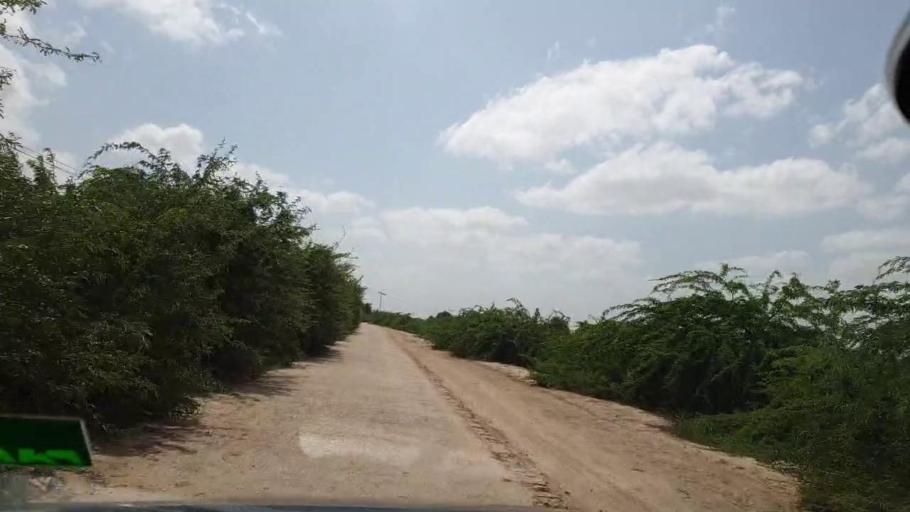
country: PK
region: Sindh
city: Kadhan
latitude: 24.5536
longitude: 69.2113
